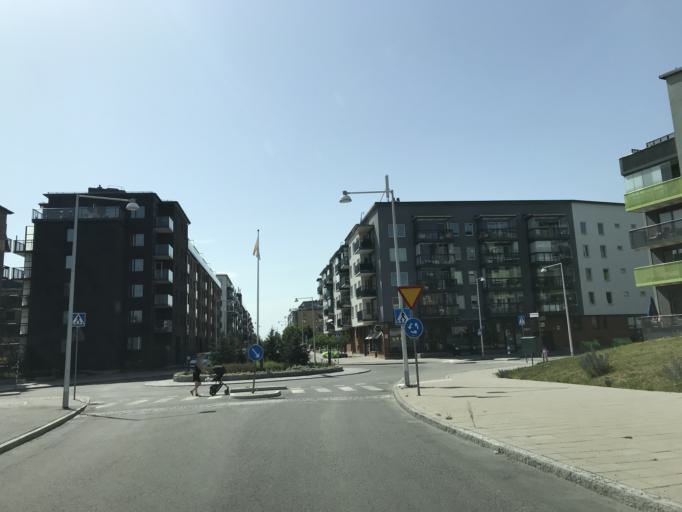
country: SE
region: Stockholm
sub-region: Solna Kommun
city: Rasunda
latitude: 59.3833
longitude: 17.9865
